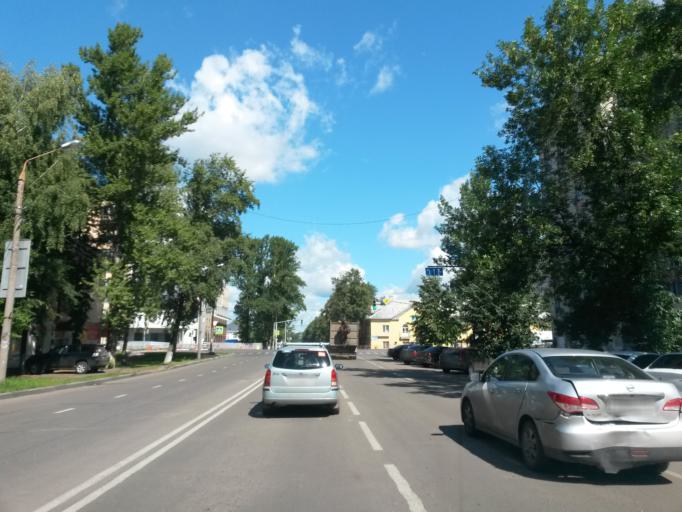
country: RU
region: Jaroslavl
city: Yaroslavl
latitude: 57.5981
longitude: 39.8784
